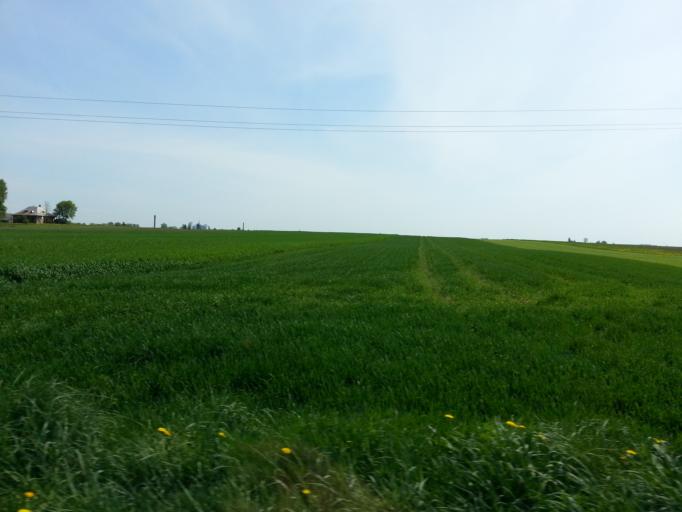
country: LT
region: Panevezys
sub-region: Panevezys City
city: Panevezys
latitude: 55.9193
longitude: 24.2355
